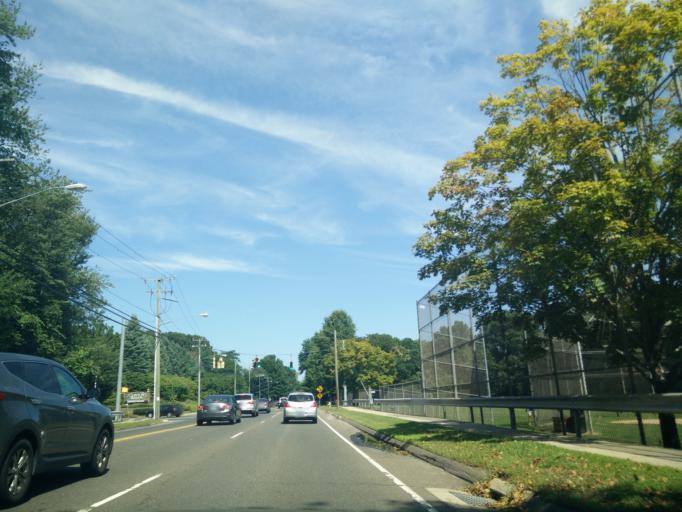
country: US
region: Connecticut
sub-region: Middlesex County
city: Clinton
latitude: 41.2924
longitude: -72.5306
